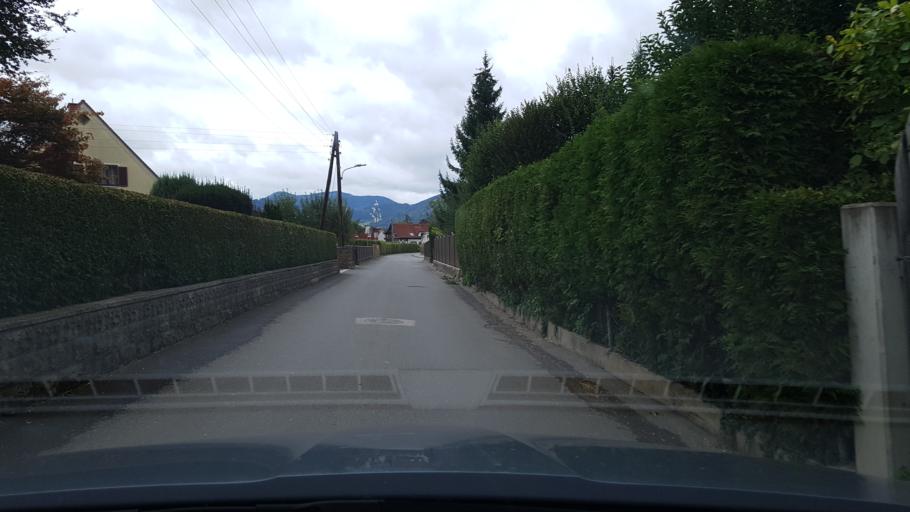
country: AT
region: Styria
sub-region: Politischer Bezirk Bruck-Muerzzuschlag
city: Sankt Marein im Muerztal
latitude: 47.4704
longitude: 15.3766
